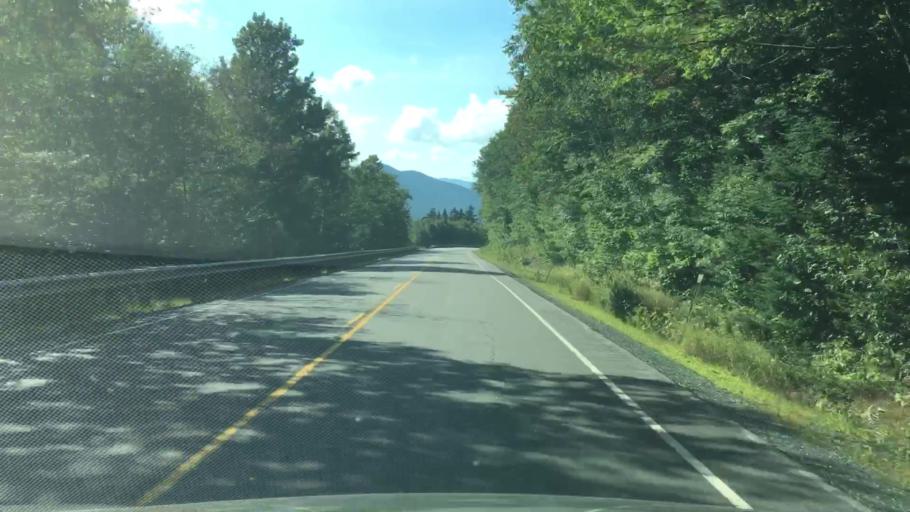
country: US
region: New Hampshire
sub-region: Grafton County
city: Woodstock
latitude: 44.0343
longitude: -71.5141
